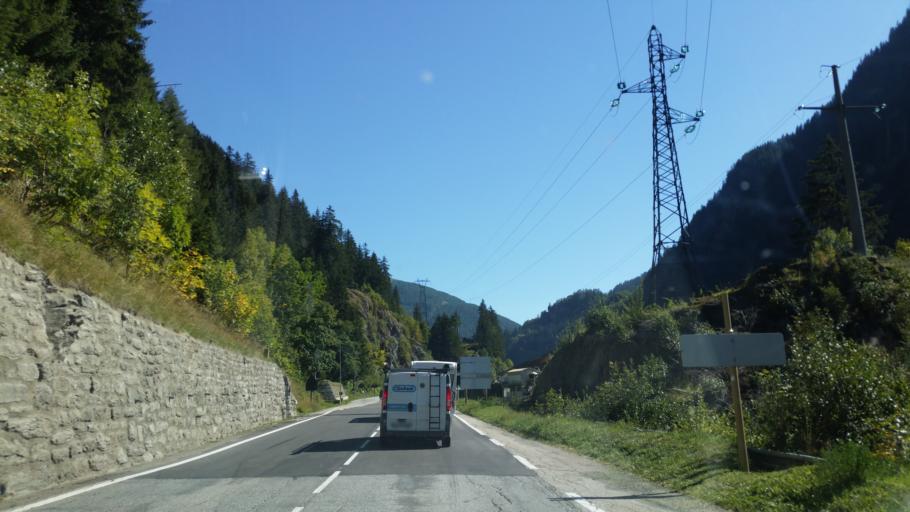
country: FR
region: Rhone-Alpes
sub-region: Departement de la Savoie
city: Tignes
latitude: 45.5629
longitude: 6.8929
